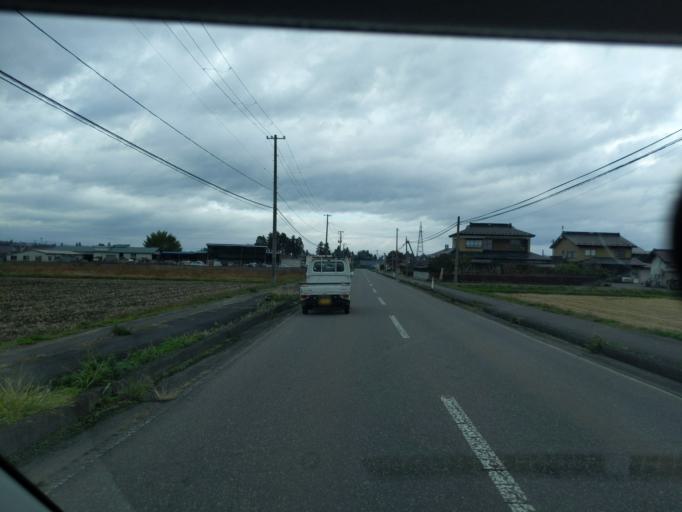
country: JP
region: Iwate
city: Mizusawa
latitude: 39.1263
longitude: 141.0674
